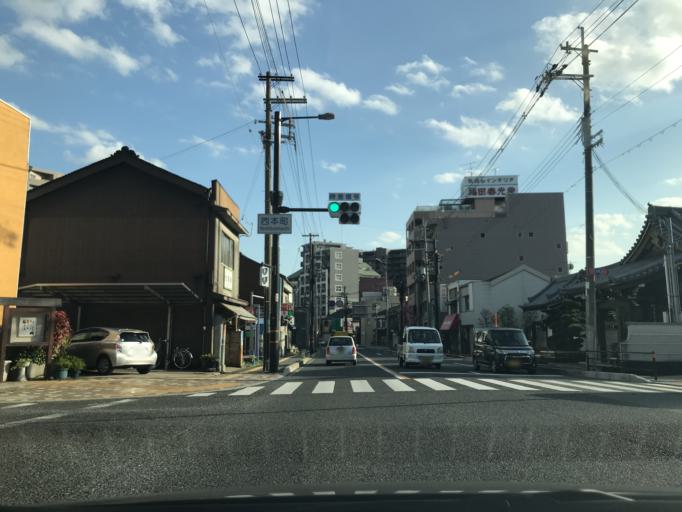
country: JP
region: Osaka
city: Ikeda
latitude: 34.8262
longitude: 135.4240
